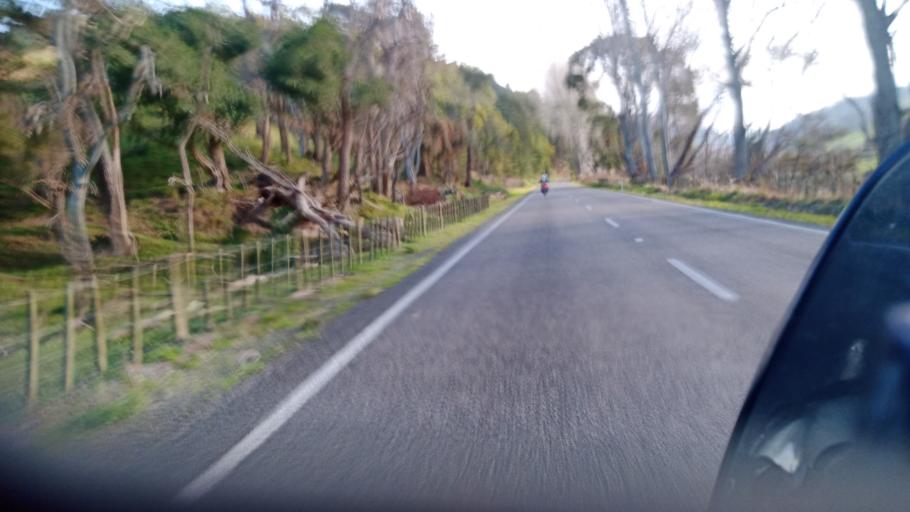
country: NZ
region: Gisborne
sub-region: Gisborne District
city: Gisborne
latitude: -38.4447
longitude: 177.6169
